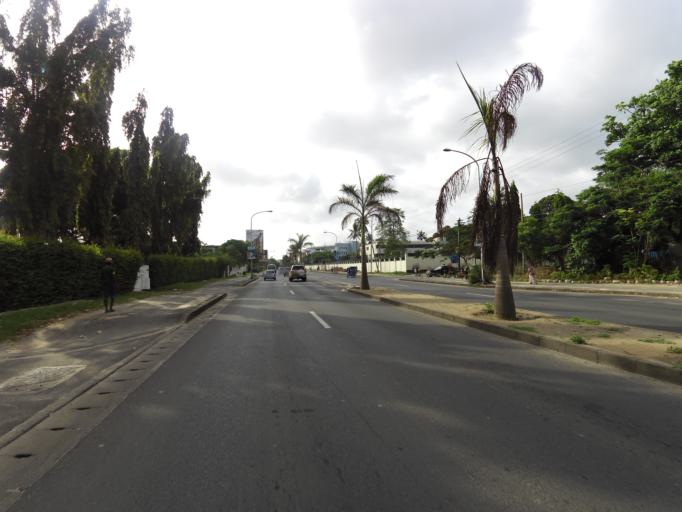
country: TZ
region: Dar es Salaam
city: Magomeni
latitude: -6.7879
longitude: 39.2785
